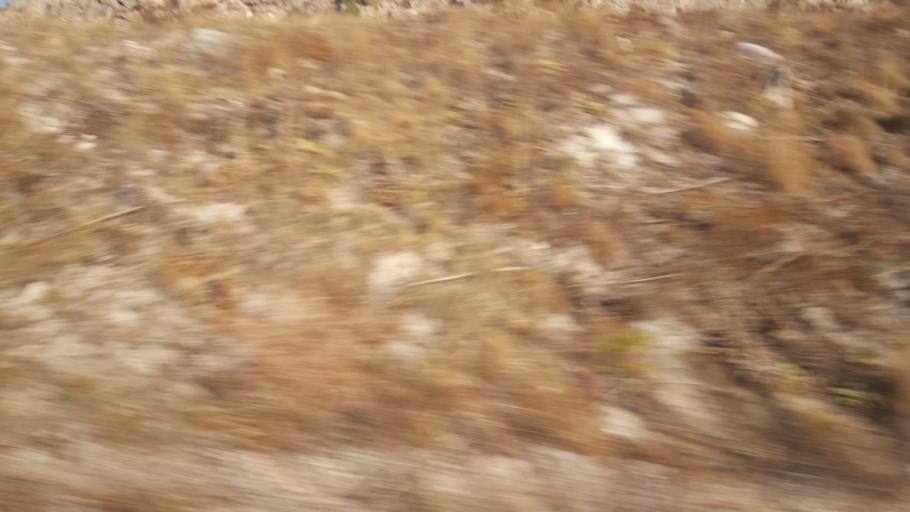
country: TR
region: Eskisehir
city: Seyitgazi
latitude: 39.4217
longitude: 30.6515
